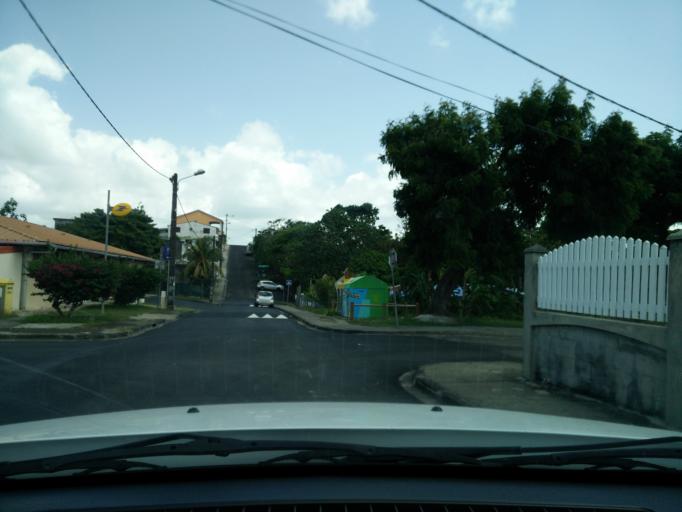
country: GP
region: Guadeloupe
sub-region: Guadeloupe
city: Petit-Canal
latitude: 16.3812
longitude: -61.4876
